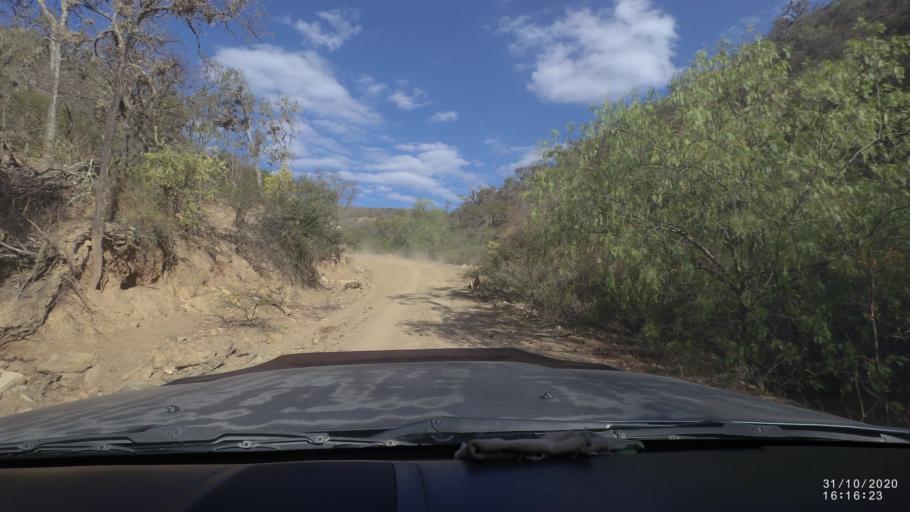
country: BO
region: Chuquisaca
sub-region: Provincia Zudanez
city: Mojocoya
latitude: -18.3900
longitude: -64.6091
